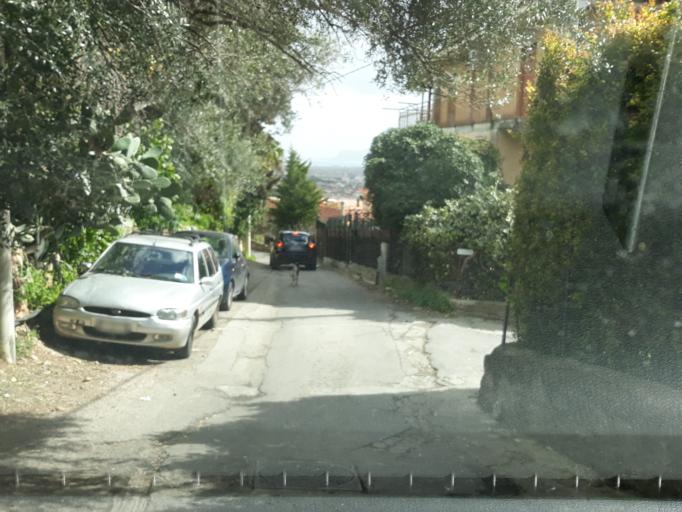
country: IT
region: Sicily
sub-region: Palermo
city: Monreale
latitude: 38.0874
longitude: 13.2995
